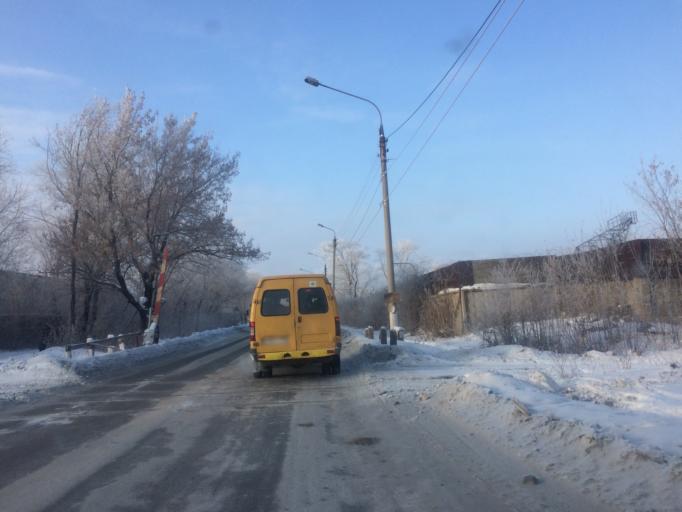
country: RU
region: Chelyabinsk
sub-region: Gorod Magnitogorsk
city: Magnitogorsk
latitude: 53.3952
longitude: 59.0738
